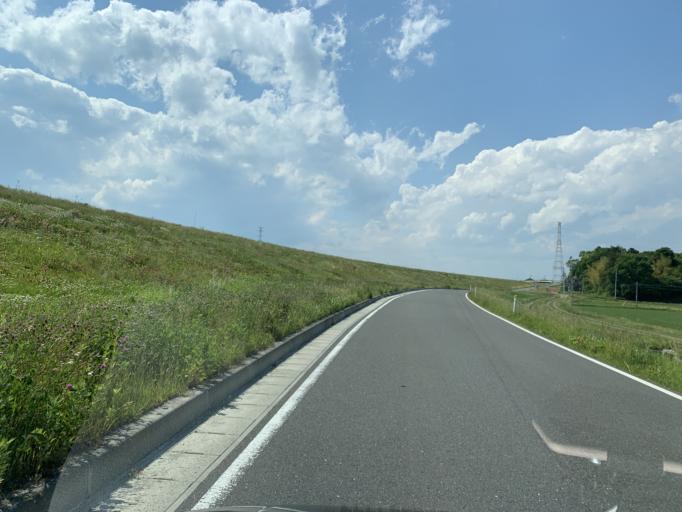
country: JP
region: Miyagi
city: Matsushima
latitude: 38.4242
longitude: 141.1283
